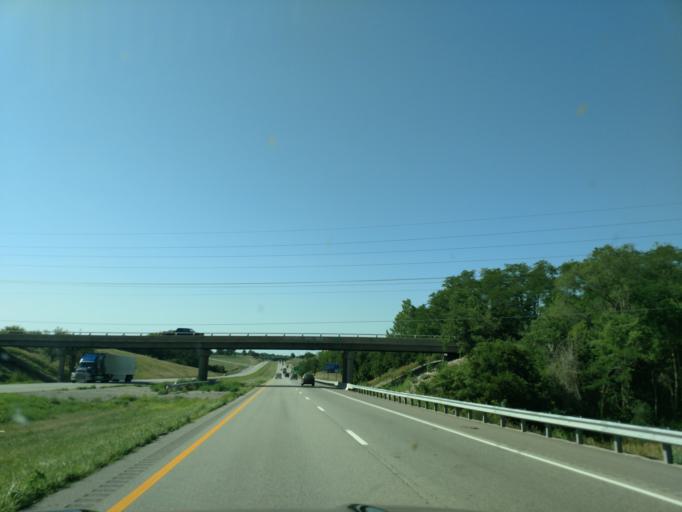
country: US
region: Missouri
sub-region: Andrew County
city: Country Club Village
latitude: 39.8060
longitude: -94.8006
